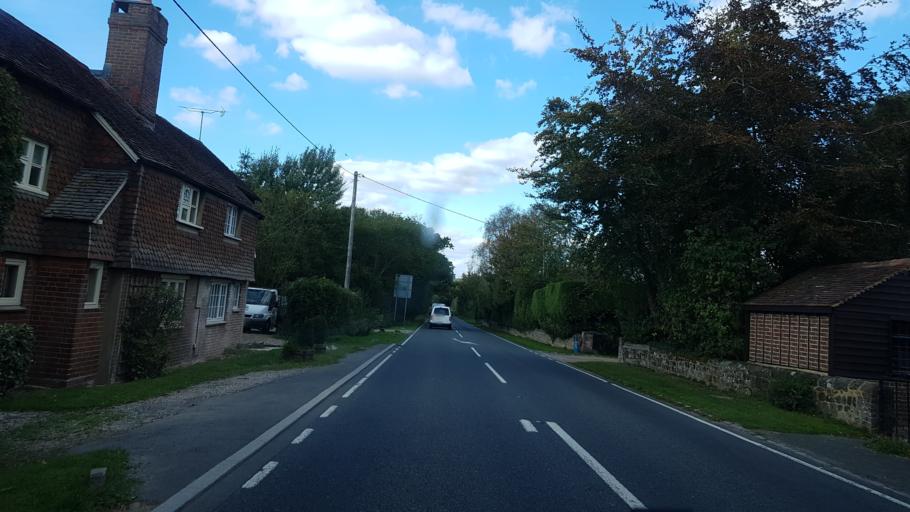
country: GB
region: England
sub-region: West Sussex
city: Petworth
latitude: 51.0447
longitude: -0.6416
